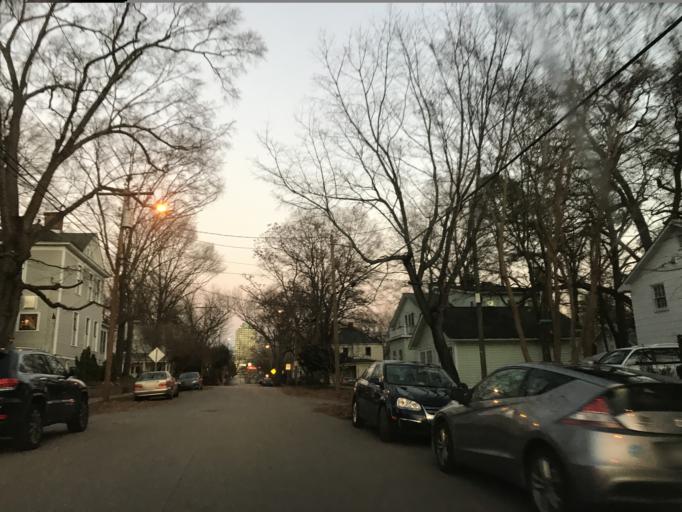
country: US
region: North Carolina
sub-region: Wake County
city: Raleigh
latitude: 35.7746
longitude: -78.6529
